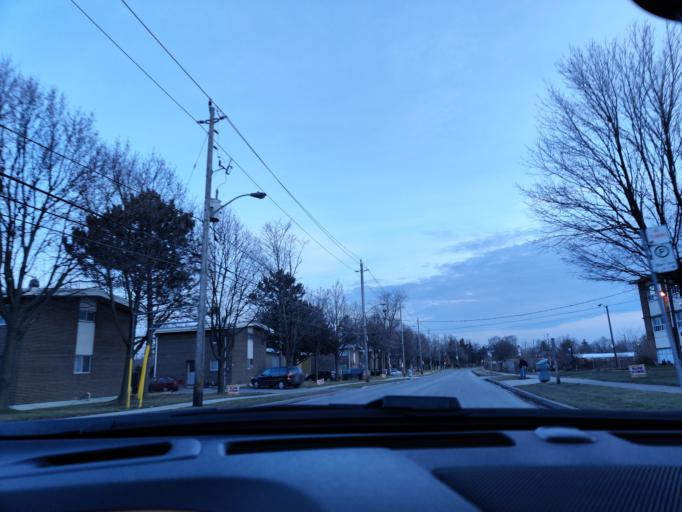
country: CA
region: Ontario
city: Toronto
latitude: 43.7198
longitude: -79.4400
